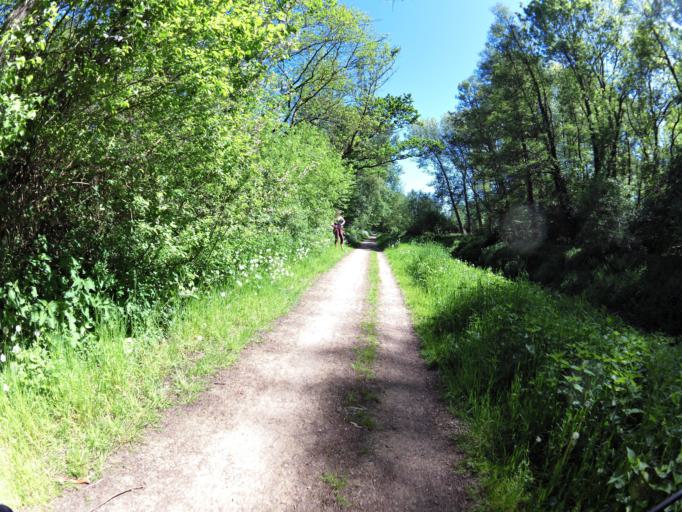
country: DE
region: North Rhine-Westphalia
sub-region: Regierungsbezirk Koln
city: Selfkant
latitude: 50.9935
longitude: 5.9399
